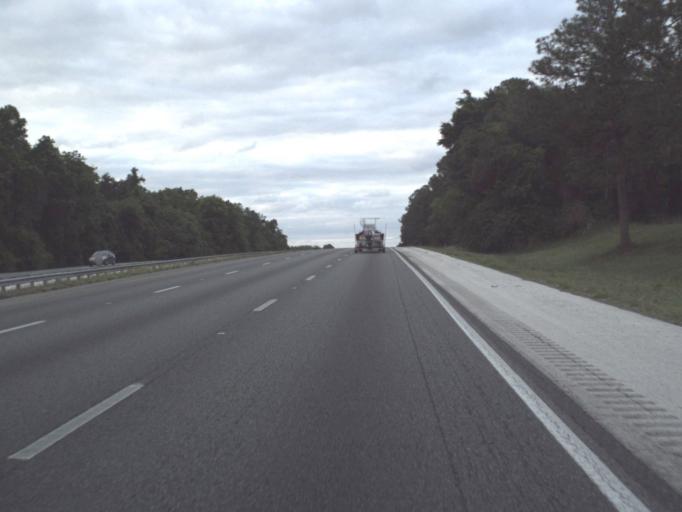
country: US
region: Florida
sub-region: Marion County
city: Ocala
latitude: 29.1160
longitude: -82.1847
